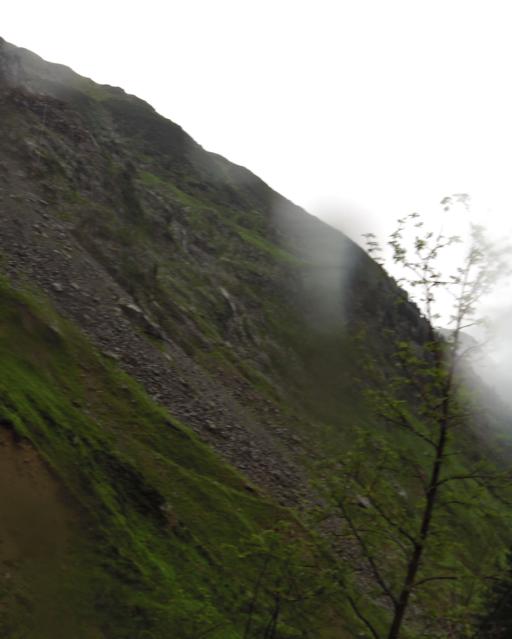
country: AT
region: Tyrol
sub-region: Politischer Bezirk Innsbruck Land
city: Neustift im Stubaital
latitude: 47.0079
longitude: 11.2222
